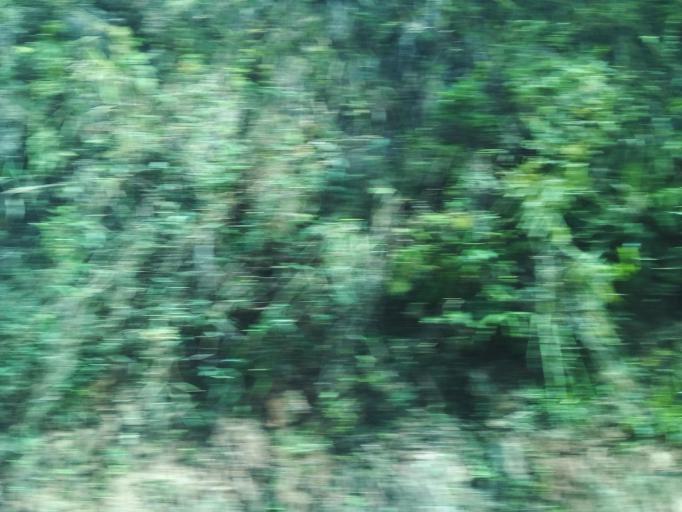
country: BR
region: Minas Gerais
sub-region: Raposos
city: Raposos
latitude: -19.8718
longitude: -43.7741
